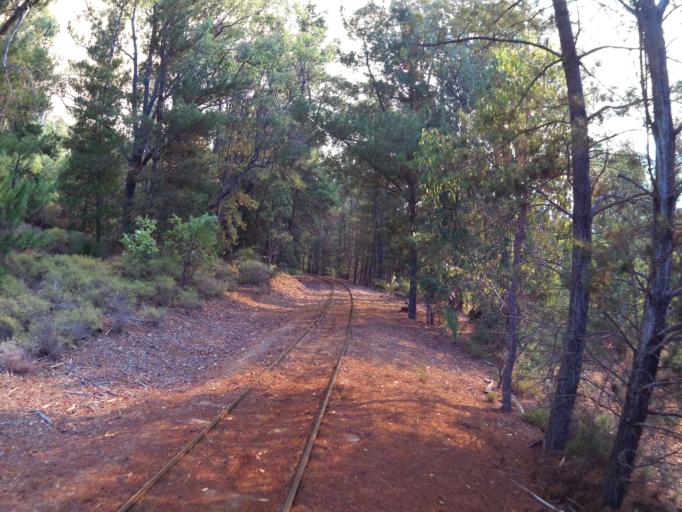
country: AU
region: Western Australia
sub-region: Waroona
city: Waroona
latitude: -32.7369
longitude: 116.1327
